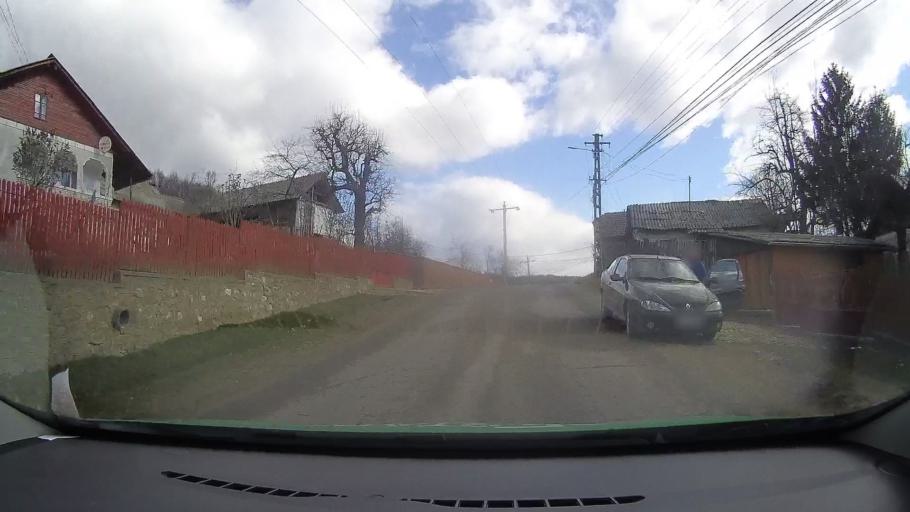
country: RO
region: Dambovita
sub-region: Comuna Buciumeni
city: Buciumeni
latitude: 45.1205
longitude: 25.4587
